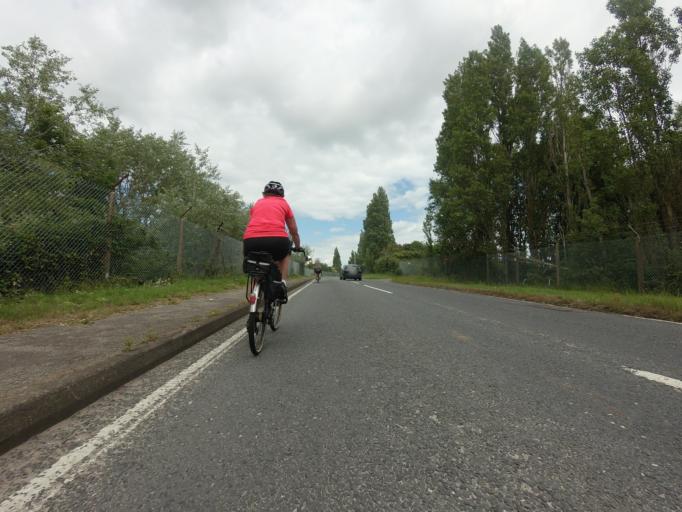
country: GB
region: England
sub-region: Medway
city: Allhallows
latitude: 51.4484
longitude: 0.6956
